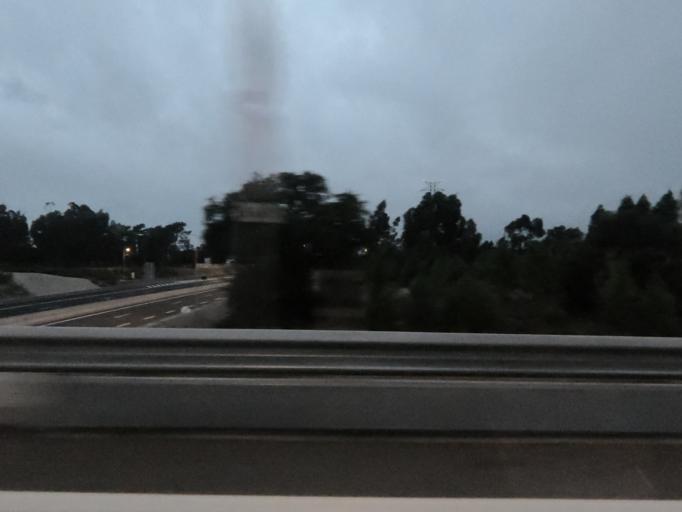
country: PT
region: Setubal
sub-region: Seixal
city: Amora
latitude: 38.6027
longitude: -9.1303
